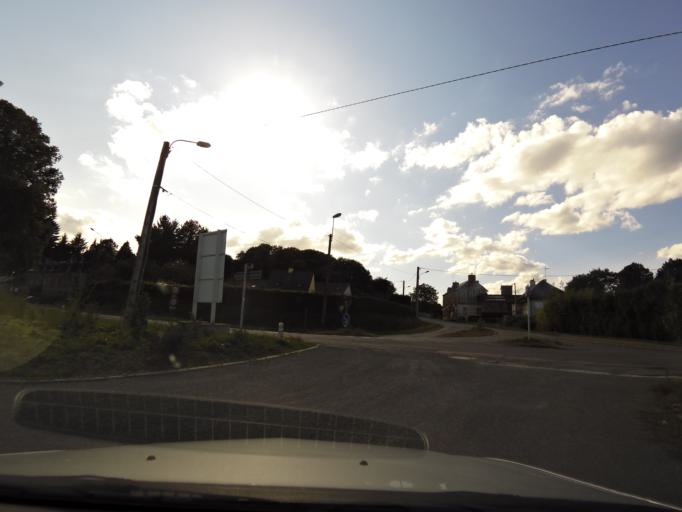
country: FR
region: Brittany
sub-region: Departement d'Ille-et-Vilaine
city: Bourg-des-Comptes
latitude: 47.9357
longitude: -1.7599
